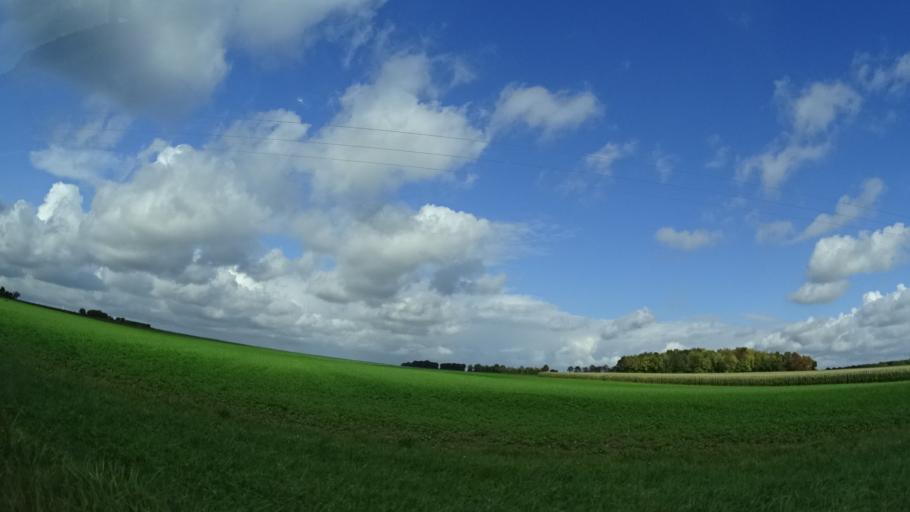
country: DE
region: Bavaria
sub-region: Regierungsbezirk Unterfranken
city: Sommerhausen
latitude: 49.7096
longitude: 10.0700
